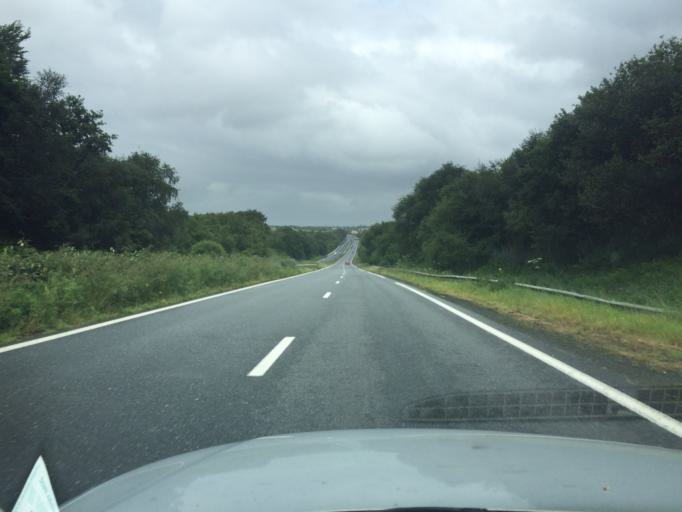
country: FR
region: Brittany
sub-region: Departement du Finistere
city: Saint-Thegonnec
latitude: 48.5260
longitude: -3.9653
